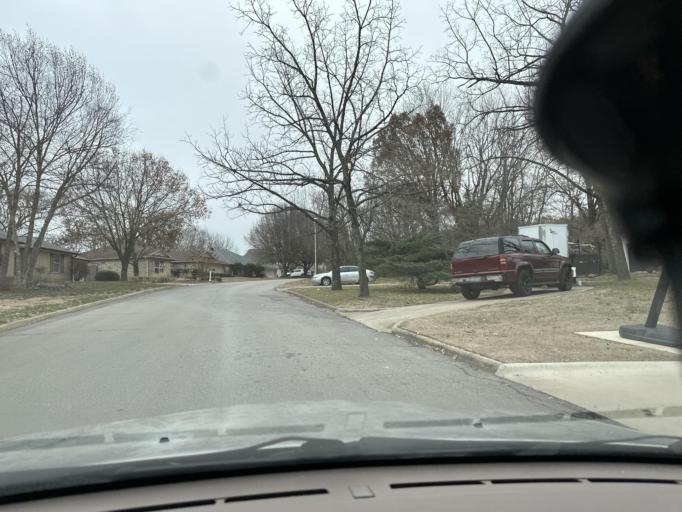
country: US
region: Arkansas
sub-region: Washington County
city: Fayetteville
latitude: 36.0834
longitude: -94.1202
